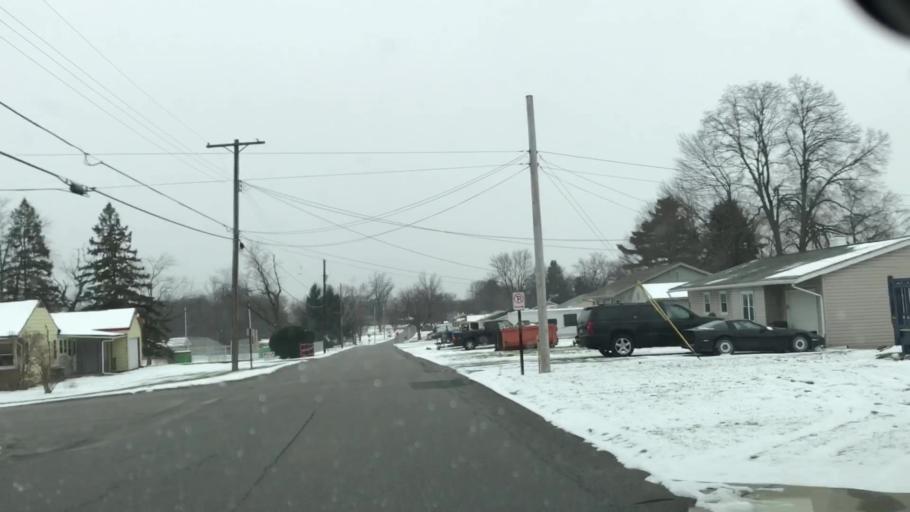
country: US
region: Pennsylvania
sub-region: Beaver County
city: Industry
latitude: 40.7012
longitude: -80.4041
